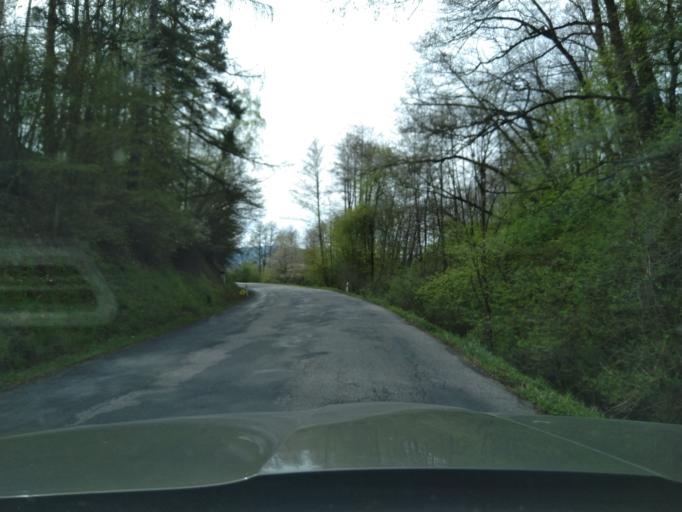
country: CZ
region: Plzensky
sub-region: Okres Klatovy
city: Susice
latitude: 49.2182
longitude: 13.6127
